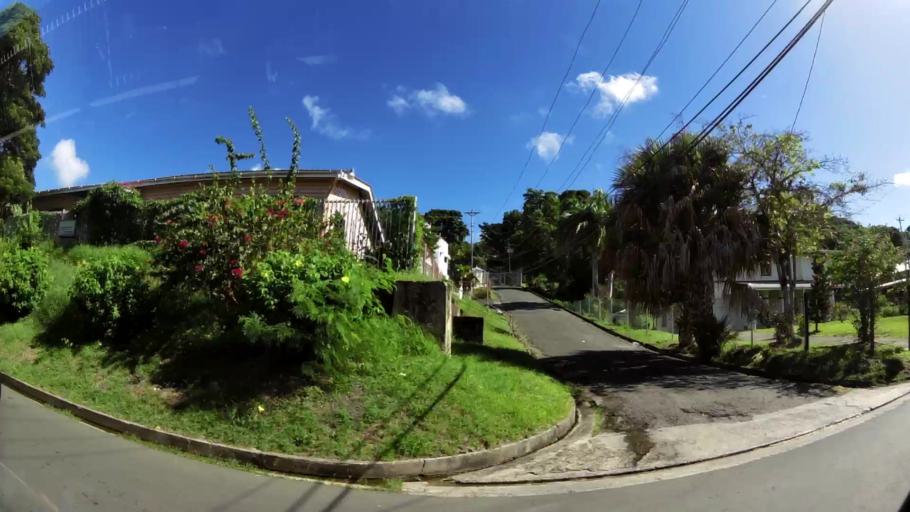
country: TT
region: Tobago
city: Scarborough
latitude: 11.1772
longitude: -60.7315
